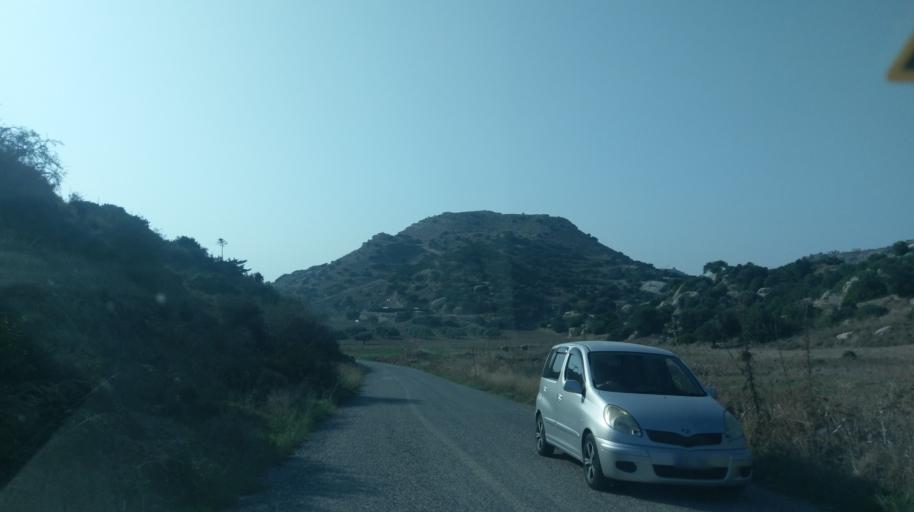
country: CY
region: Ammochostos
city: Rizokarpaso
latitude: 35.5193
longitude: 34.3166
